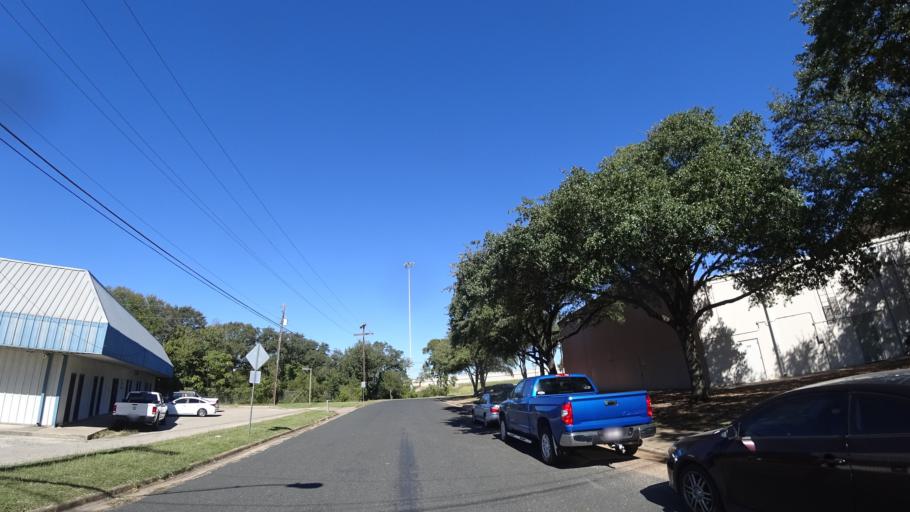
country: US
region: Texas
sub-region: Travis County
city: Rollingwood
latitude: 30.2305
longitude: -97.8034
